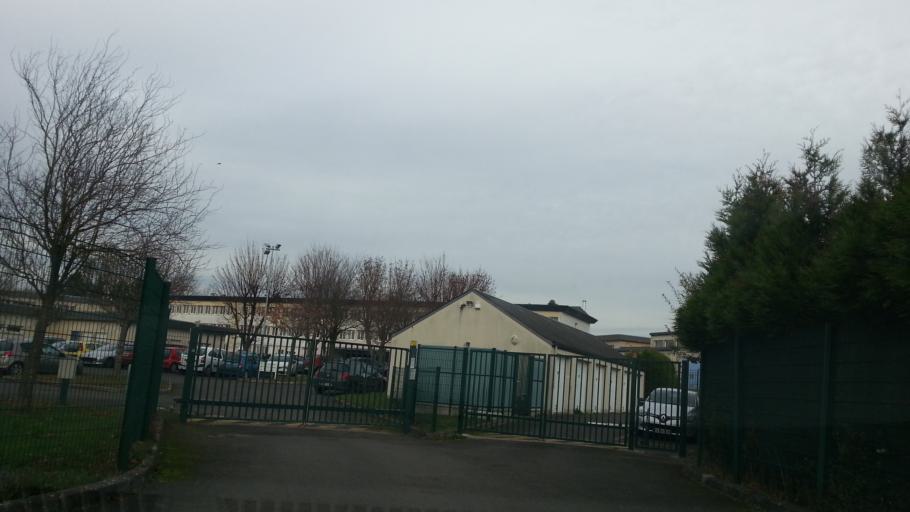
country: FR
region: Picardie
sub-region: Departement de l'Oise
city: Montataire
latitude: 49.2597
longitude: 2.4379
